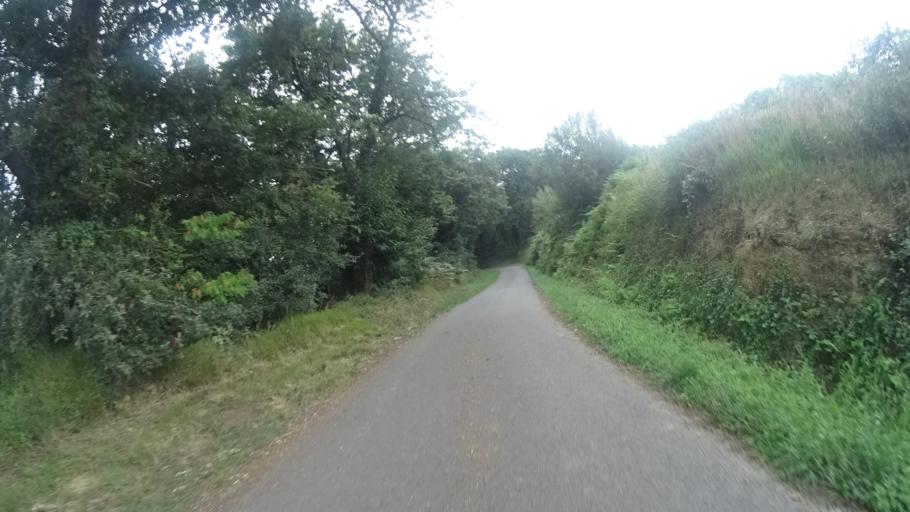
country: FR
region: Aquitaine
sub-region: Departement des Pyrenees-Atlantiques
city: Orthez
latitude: 43.4953
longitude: -0.7004
